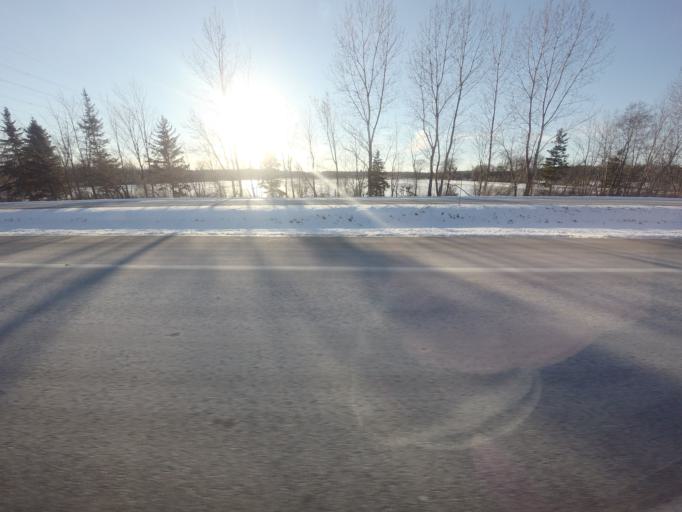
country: CA
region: Ontario
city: Bells Corners
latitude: 45.3103
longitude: -75.7998
